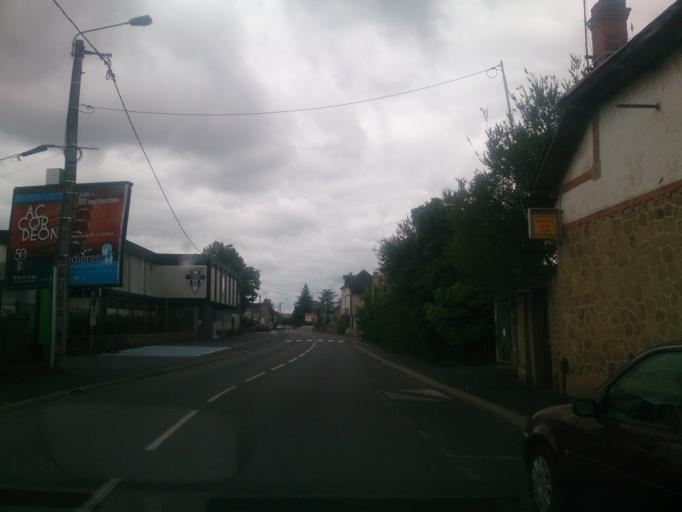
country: FR
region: Limousin
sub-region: Departement de la Correze
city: Malemort-sur-Correze
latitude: 45.1632
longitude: 1.5491
